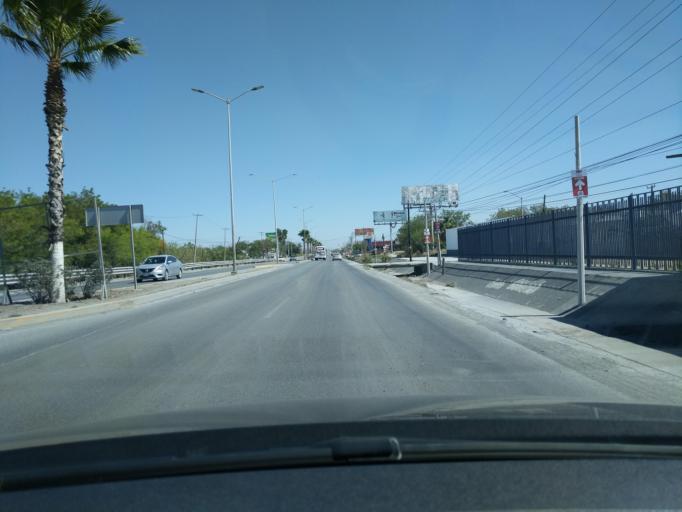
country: MX
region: Nuevo Leon
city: Juarez
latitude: 25.6399
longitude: -100.0880
